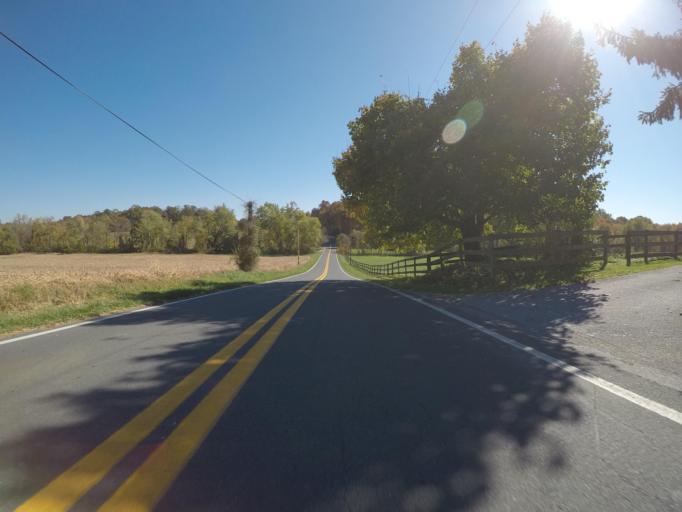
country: US
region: Maryland
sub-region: Carroll County
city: Hampstead
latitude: 39.5611
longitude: -76.8498
